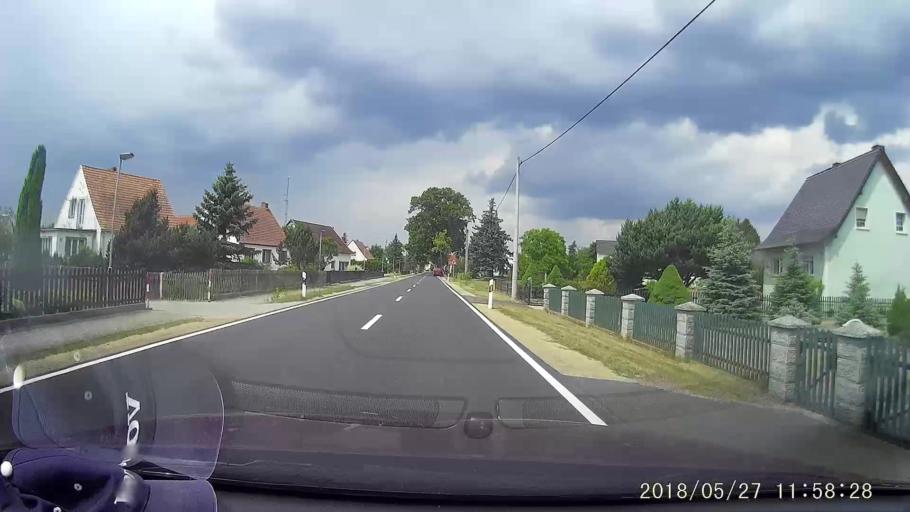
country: DE
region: Saxony
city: Mucka
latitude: 51.3133
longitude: 14.7094
